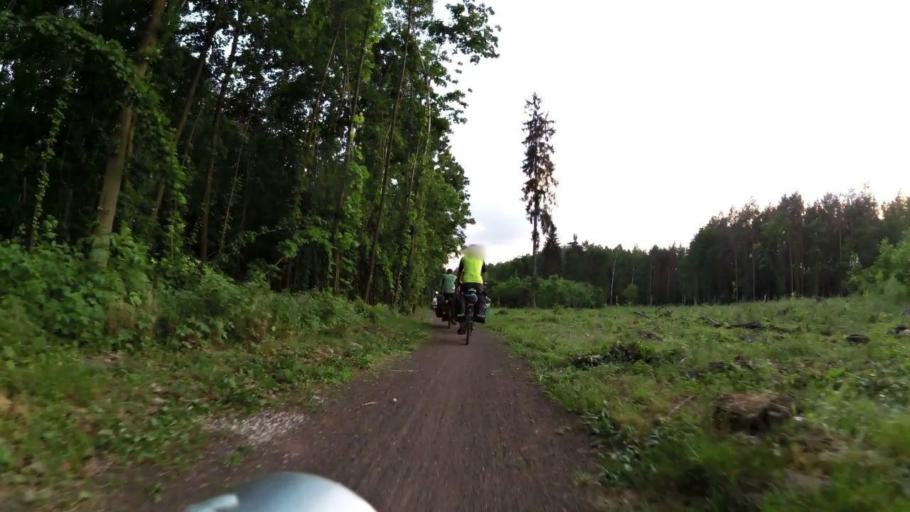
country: PL
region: Kujawsko-Pomorskie
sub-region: Powiat bydgoski
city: Dabrowa Chelminska
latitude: 53.1697
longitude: 18.2621
